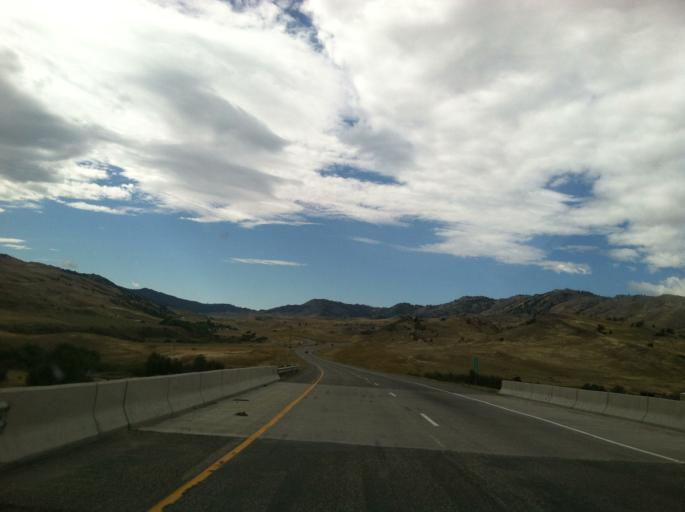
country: US
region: Montana
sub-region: Park County
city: Livingston
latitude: 45.6630
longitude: -110.6717
